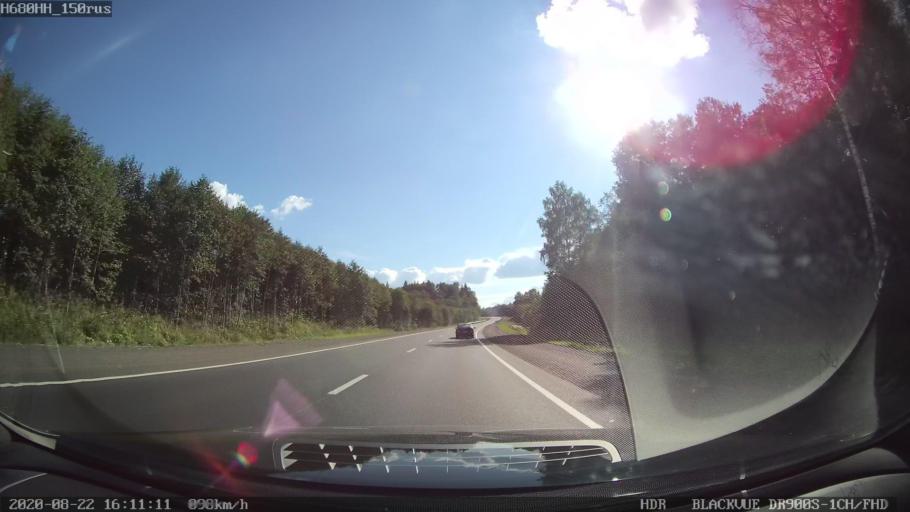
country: RU
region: Tverskaya
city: Rameshki
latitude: 57.5042
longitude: 36.2650
